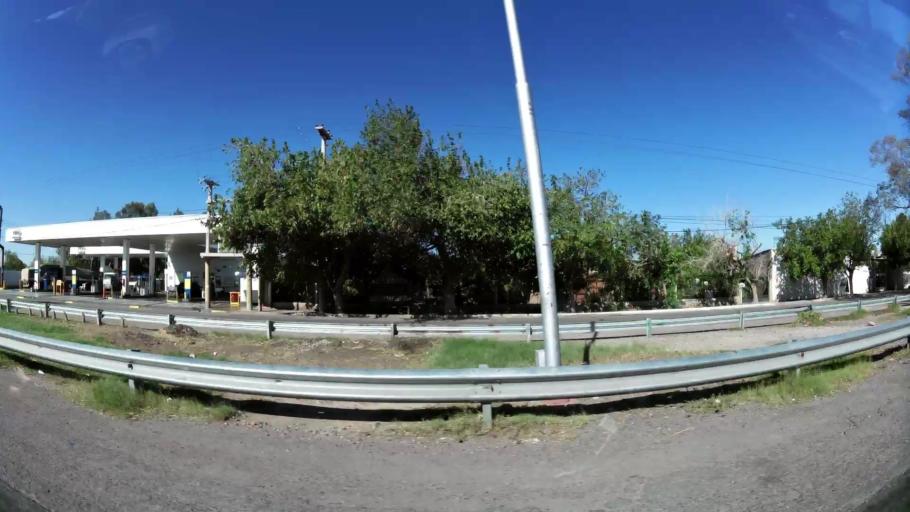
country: AR
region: San Juan
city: Villa Paula de Sarmiento
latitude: -31.5102
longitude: -68.5174
